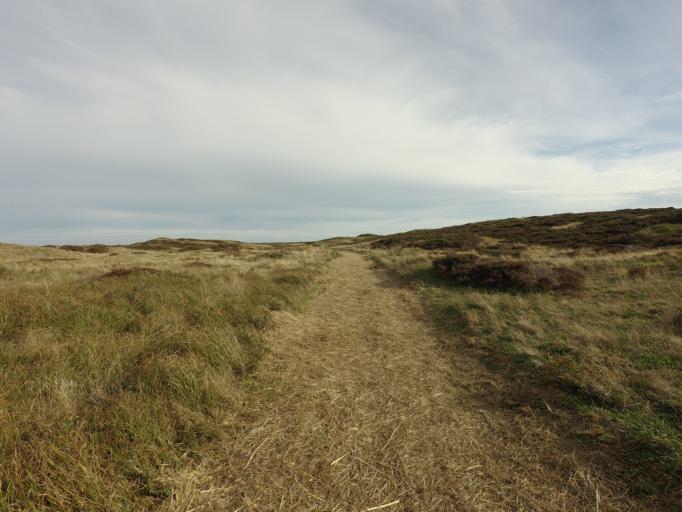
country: NL
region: North Holland
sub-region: Gemeente Den Helder
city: Den Helder
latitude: 53.0150
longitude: 4.7412
